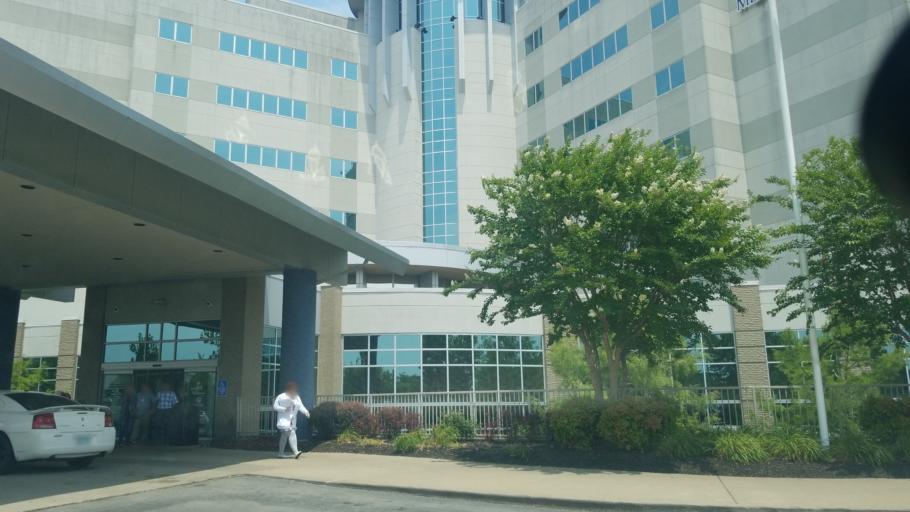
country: US
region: Tennessee
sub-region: Davidson County
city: Nashville
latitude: 36.2445
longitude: -86.7497
